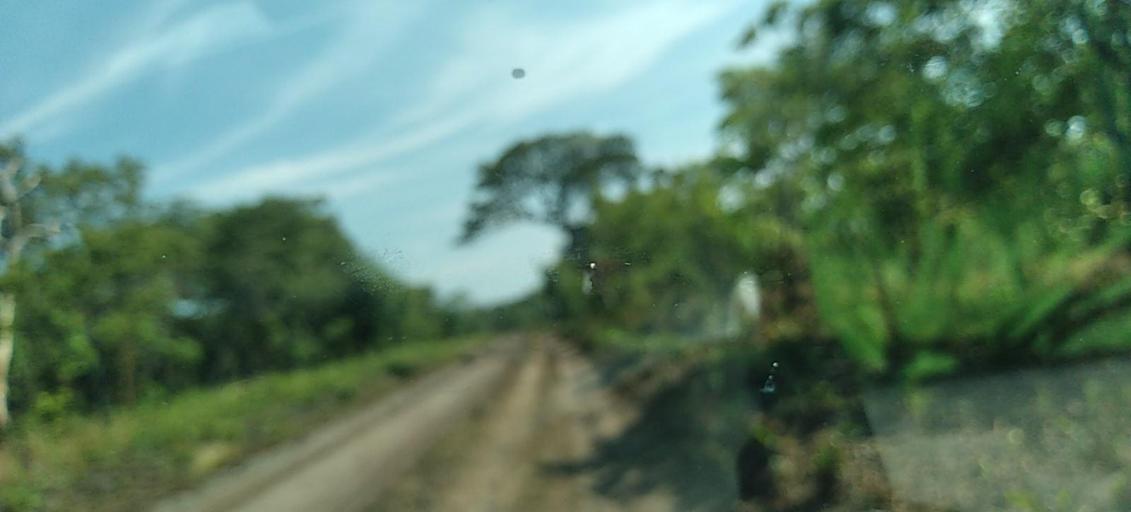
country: ZM
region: North-Western
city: Mwinilunga
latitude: -11.7962
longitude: 25.1674
